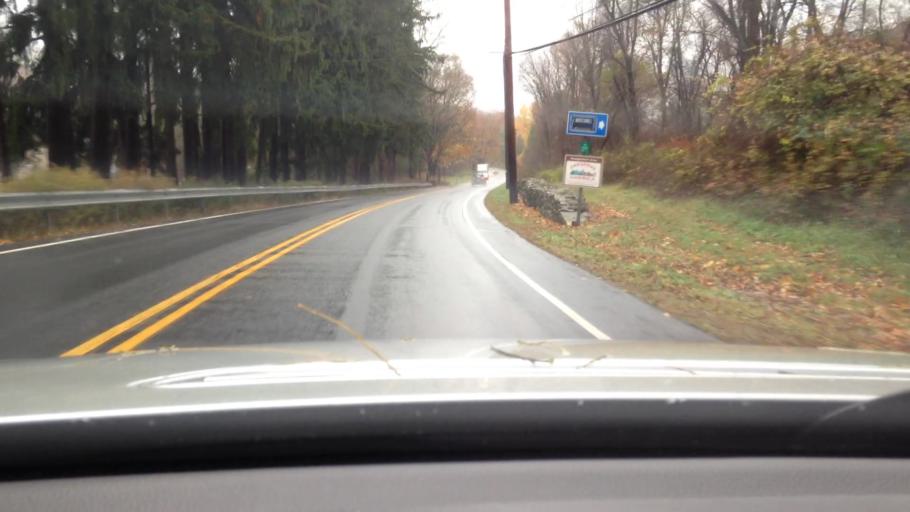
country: US
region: New York
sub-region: Putnam County
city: Cold Spring
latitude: 41.4162
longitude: -73.9388
